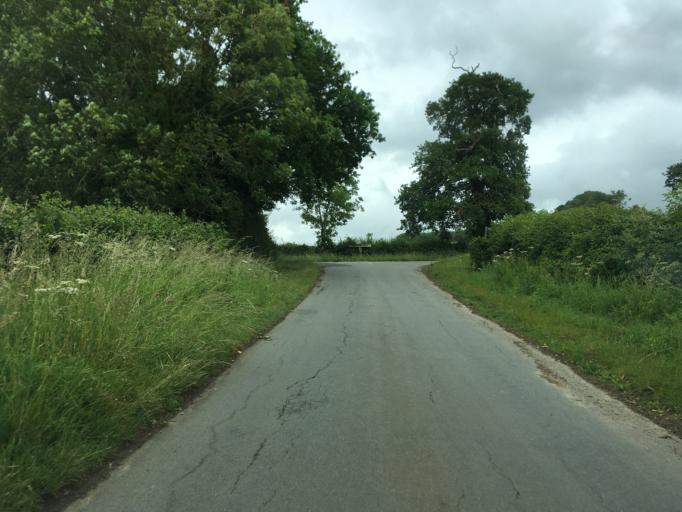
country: GB
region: England
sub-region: Gloucestershire
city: Mickleton
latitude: 52.0729
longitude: -1.7458
